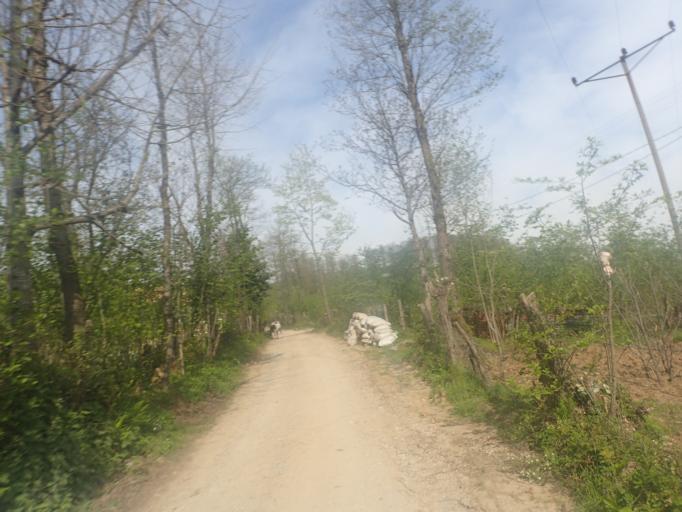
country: TR
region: Ordu
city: Catalpinar
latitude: 40.8817
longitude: 37.4911
